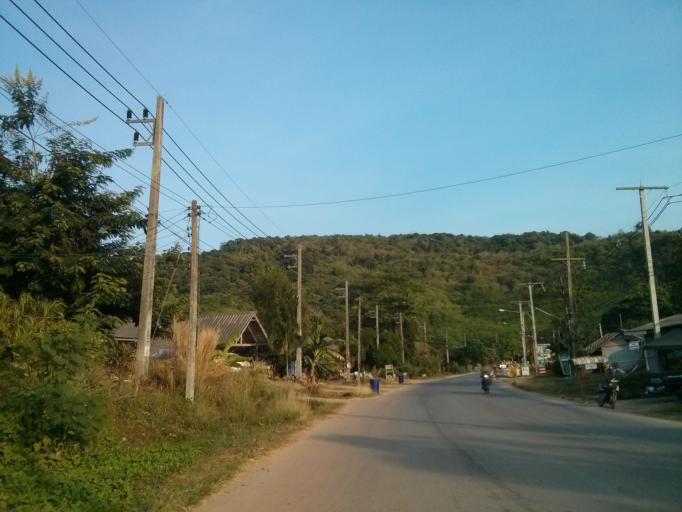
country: TH
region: Krabi
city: Saladan
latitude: 7.5671
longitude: 99.0399
